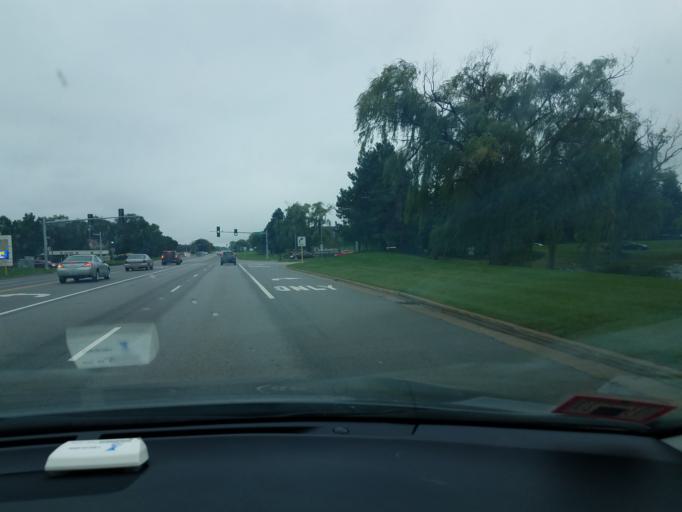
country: US
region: Illinois
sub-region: Lake County
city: Lincolnshire
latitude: 42.1955
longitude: -87.9311
